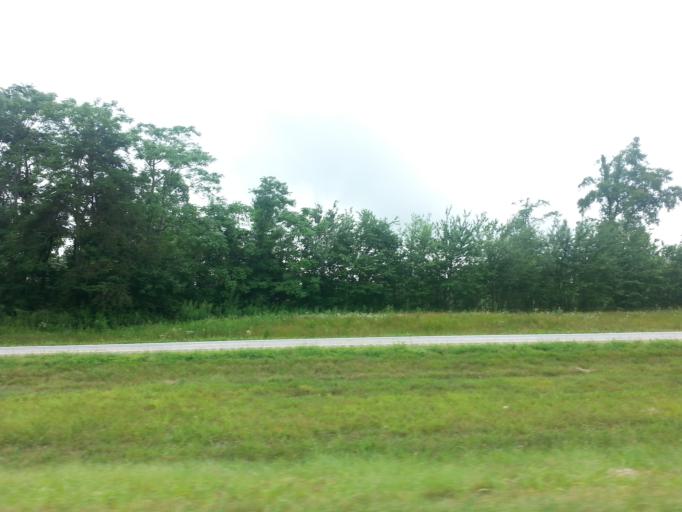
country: US
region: Tennessee
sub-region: Putnam County
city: Monterey
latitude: 36.0938
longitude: -85.2302
